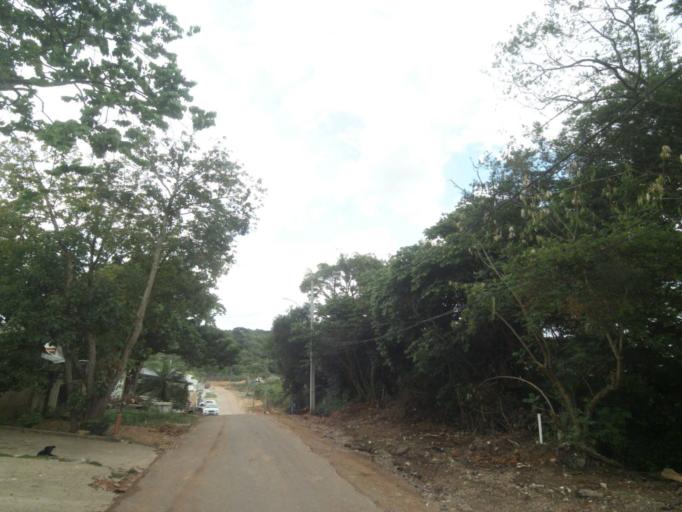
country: BR
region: Parana
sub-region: Curitiba
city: Curitiba
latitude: -25.4661
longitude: -49.3412
